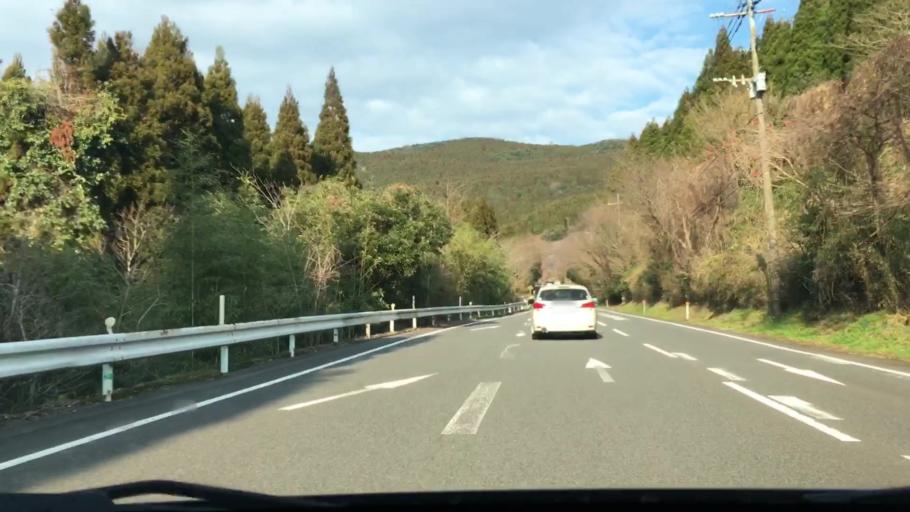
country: JP
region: Miyazaki
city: Miyazaki-shi
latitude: 31.7726
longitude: 131.3301
